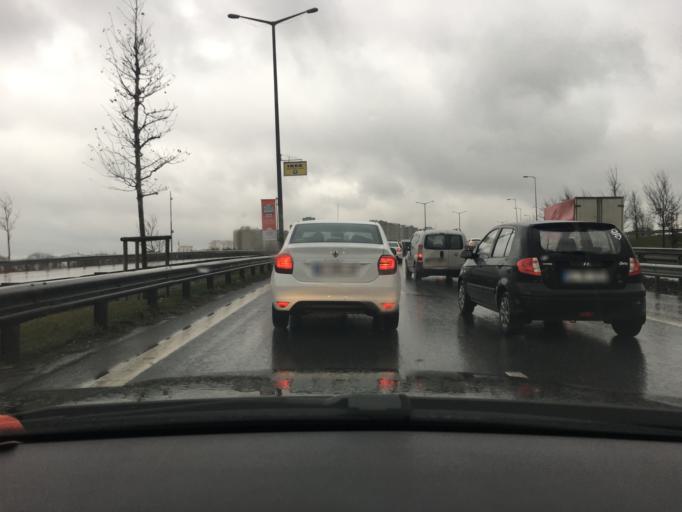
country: TR
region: Istanbul
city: Esenler
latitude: 41.0431
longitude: 28.8853
